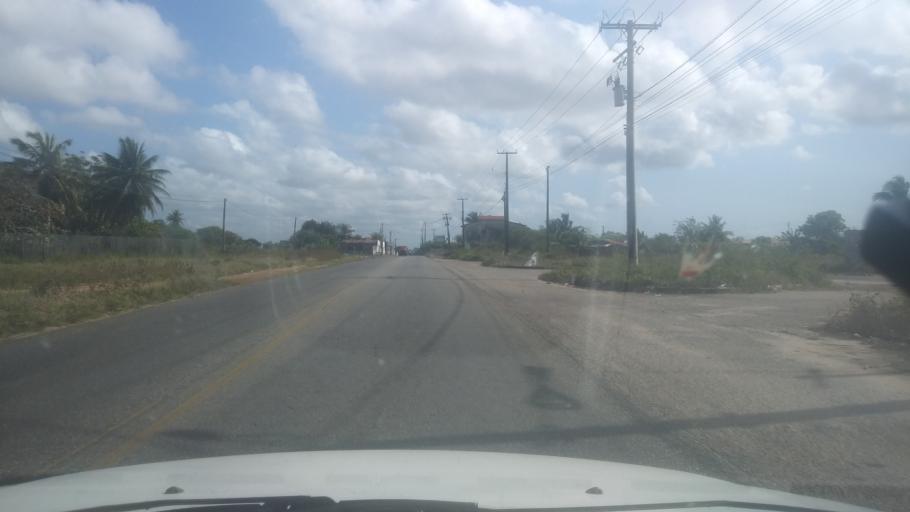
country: BR
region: Rio Grande do Norte
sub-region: Extremoz
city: Extremoz
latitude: -5.7153
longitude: -35.2775
